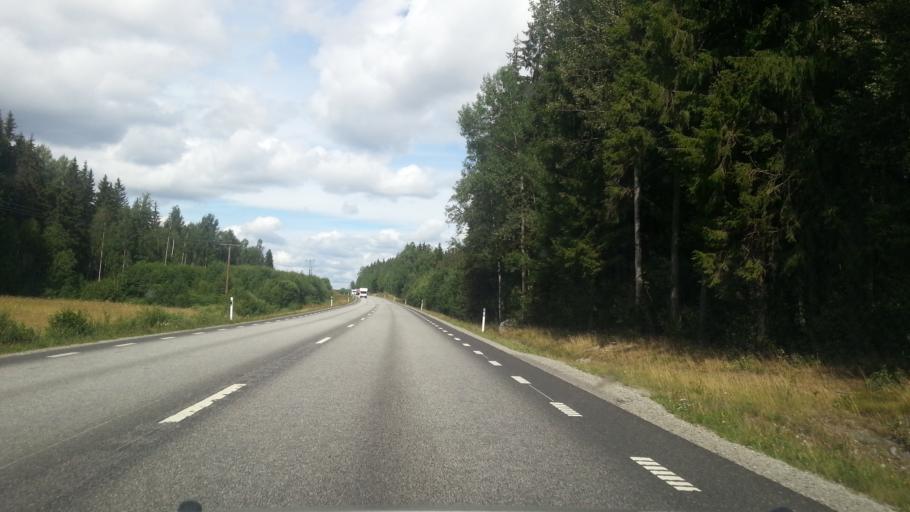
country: SE
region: OErebro
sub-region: Lindesbergs Kommun
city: Lindesberg
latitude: 59.5773
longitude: 15.2040
